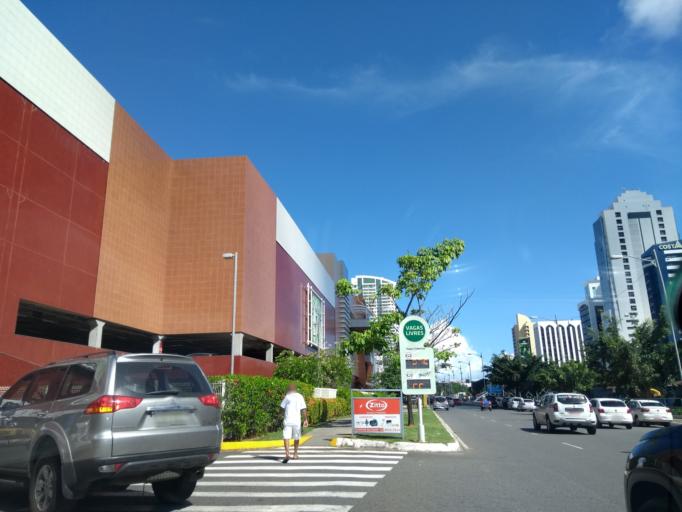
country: BR
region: Bahia
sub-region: Salvador
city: Salvador
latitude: -12.9782
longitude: -38.4566
